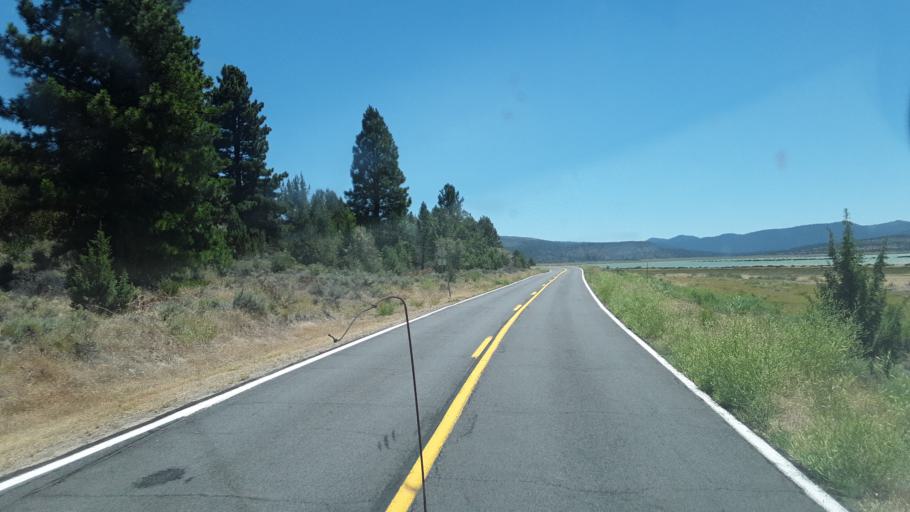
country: US
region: California
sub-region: Lassen County
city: Susanville
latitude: 40.6876
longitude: -120.6627
